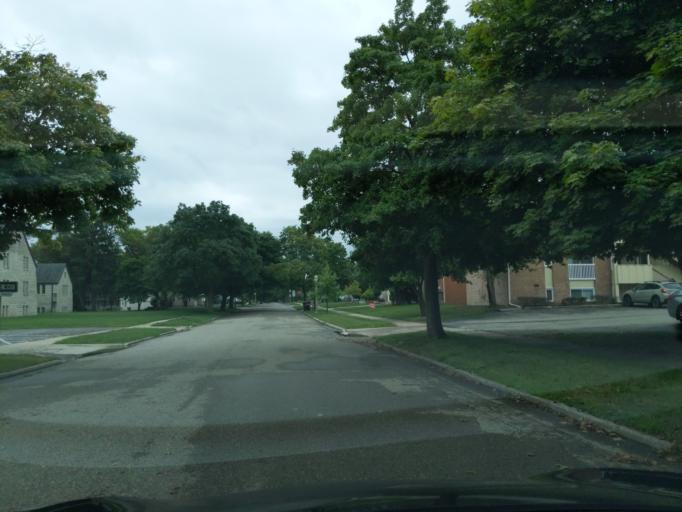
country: US
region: Michigan
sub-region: Ingham County
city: Lansing
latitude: 42.6911
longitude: -84.5368
